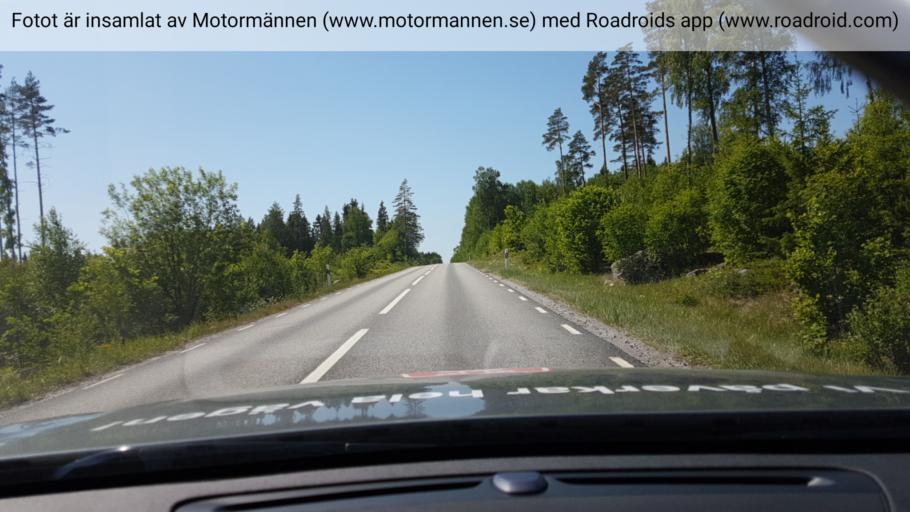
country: SE
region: Stockholm
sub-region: Norrtalje Kommun
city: Rimbo
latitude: 59.7682
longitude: 18.4212
